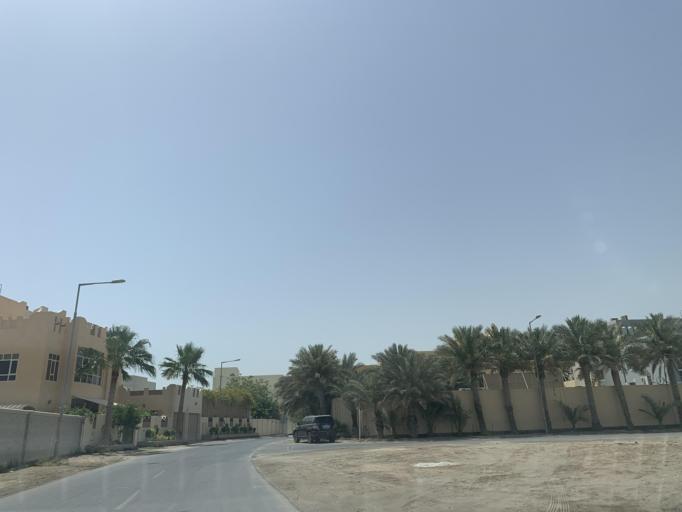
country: BH
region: Northern
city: Sitrah
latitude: 26.1551
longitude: 50.5841
